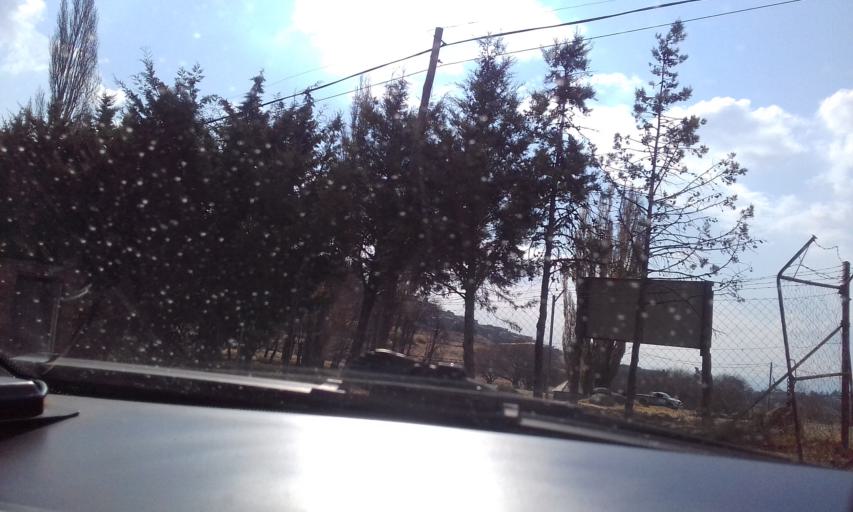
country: LS
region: Thaba-Tseka
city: Thaba-Tseka
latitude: -29.5238
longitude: 28.6032
